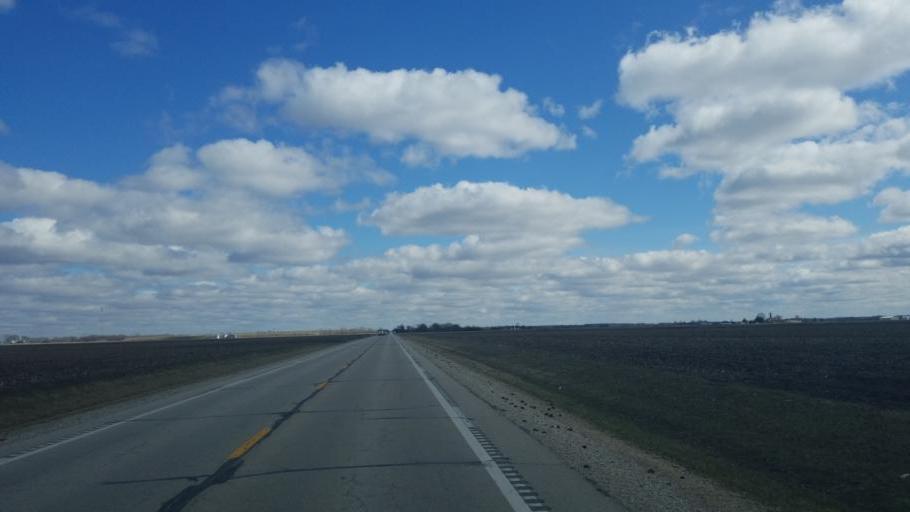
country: US
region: Illinois
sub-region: Douglas County
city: Villa Grove
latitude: 39.7921
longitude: -88.0811
